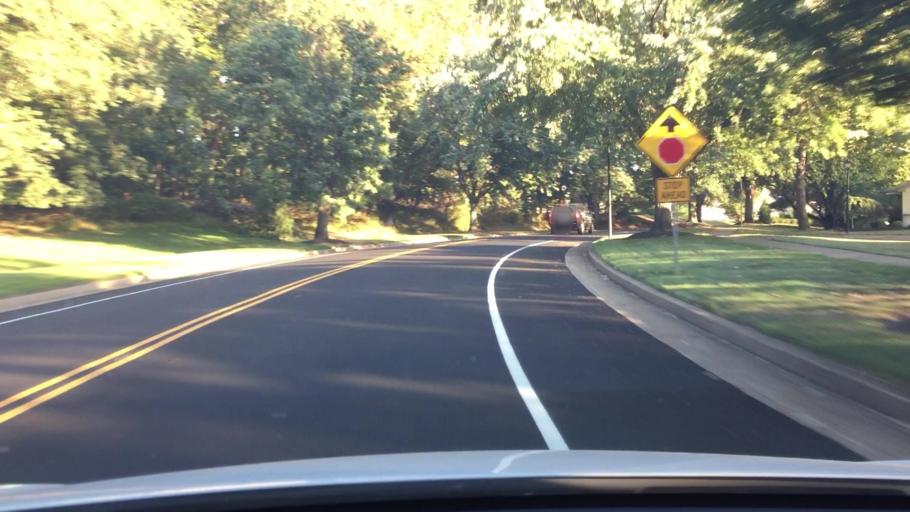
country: US
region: Pennsylvania
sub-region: Bucks County
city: Newtown
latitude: 40.2199
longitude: -74.9517
